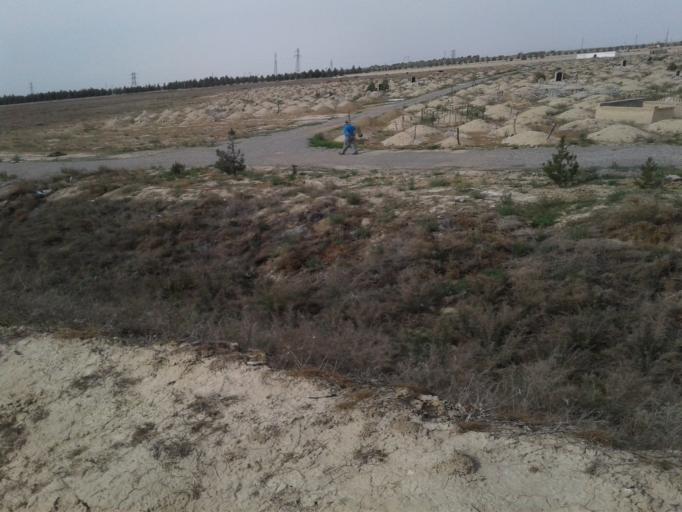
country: TM
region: Ahal
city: Abadan
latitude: 38.1727
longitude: 57.9712
